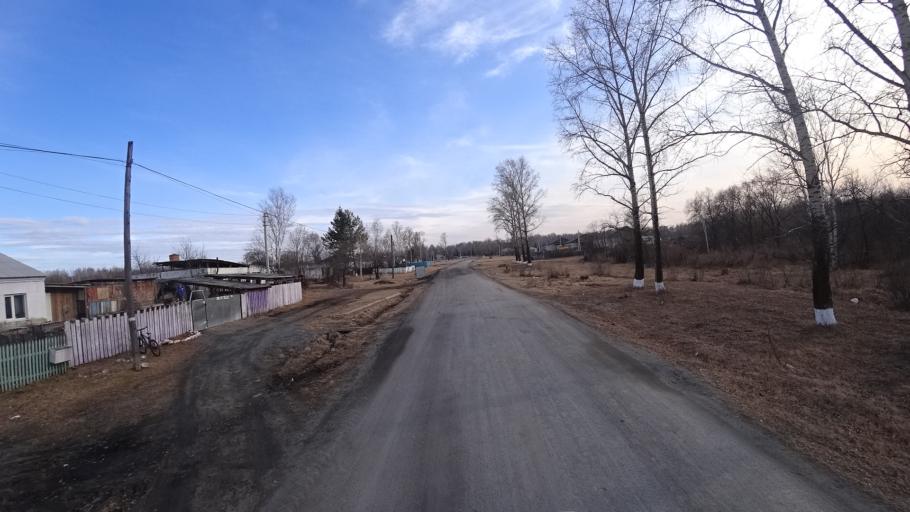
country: RU
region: Amur
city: Bureya
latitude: 50.0183
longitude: 129.7683
